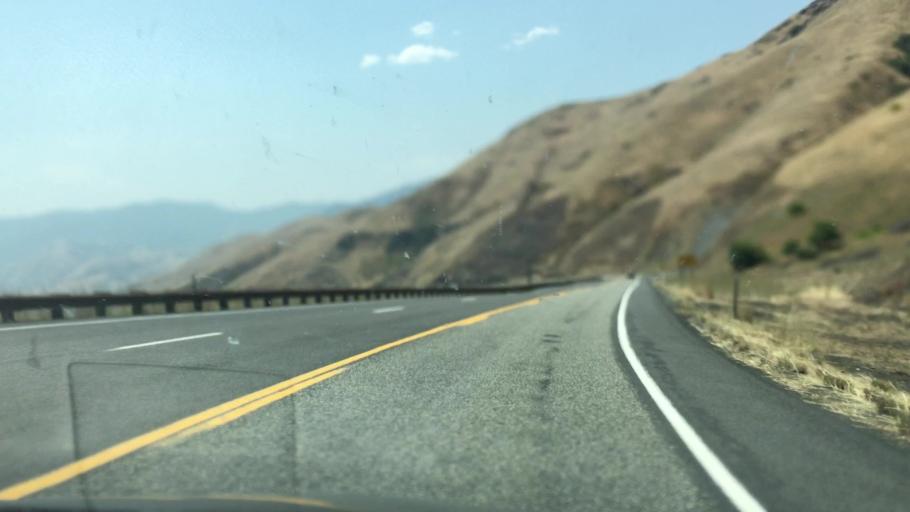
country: US
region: Idaho
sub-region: Idaho County
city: Grangeville
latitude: 45.8064
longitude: -116.2820
